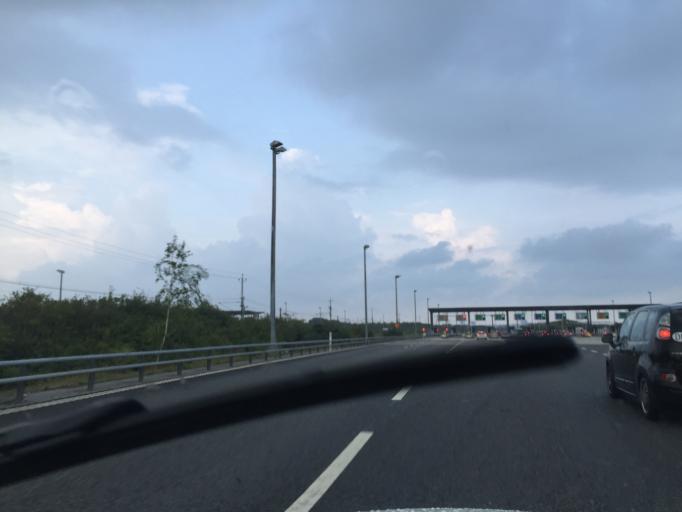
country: SE
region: Skane
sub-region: Malmo
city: Bunkeflostrand
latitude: 55.5648
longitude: 12.9099
